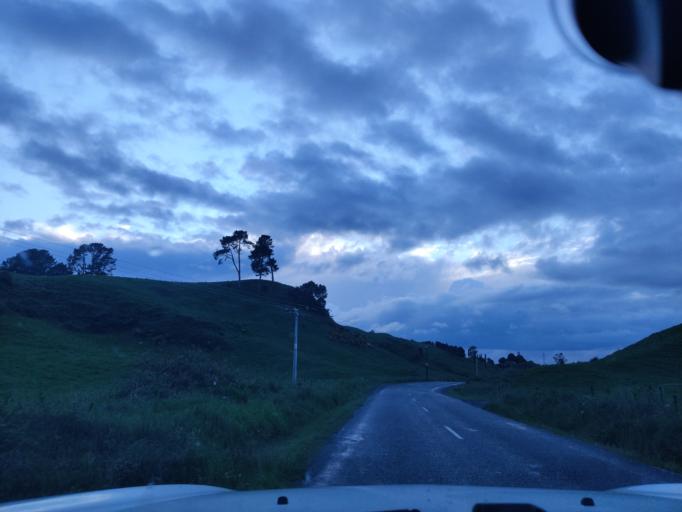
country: NZ
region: Waikato
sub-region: South Waikato District
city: Tokoroa
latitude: -38.1962
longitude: 175.8043
